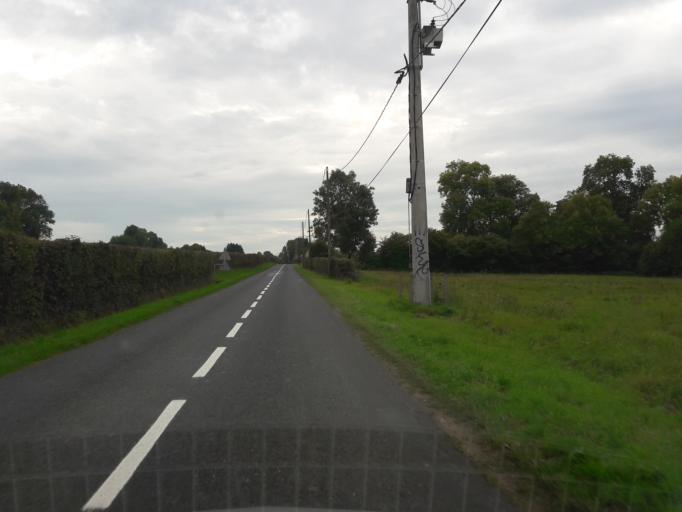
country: FR
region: Lower Normandy
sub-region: Departement du Calvados
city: Cahagnes
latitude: 49.1586
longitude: -0.7294
